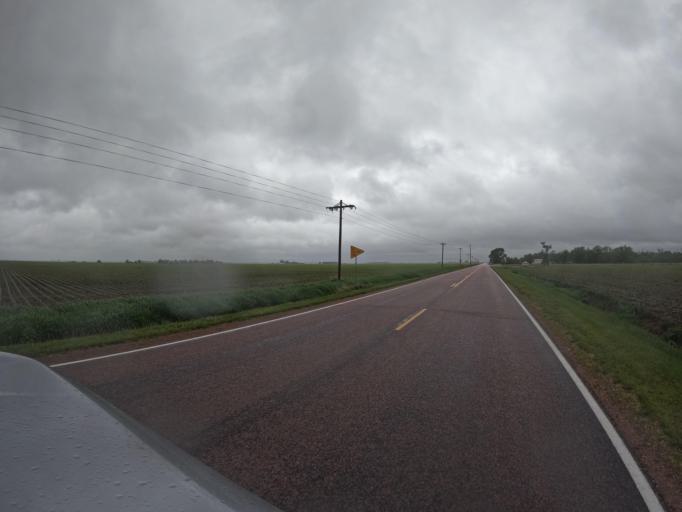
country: US
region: Nebraska
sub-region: Clay County
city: Harvard
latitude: 40.6115
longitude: -98.0954
